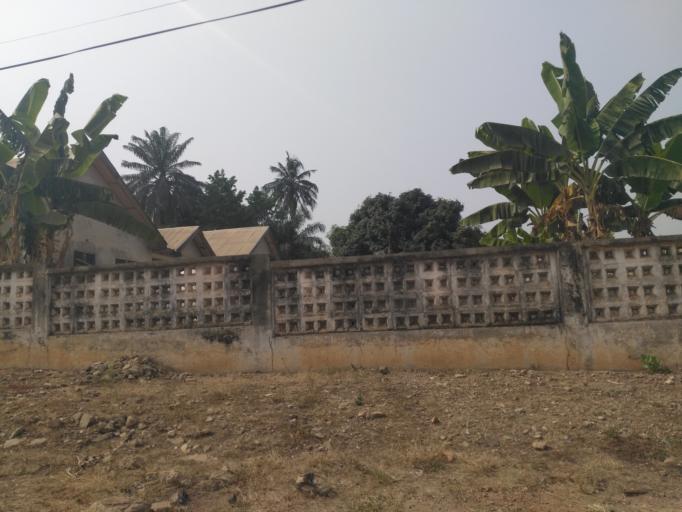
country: GH
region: Ashanti
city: Kumasi
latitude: 6.6741
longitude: -1.6008
